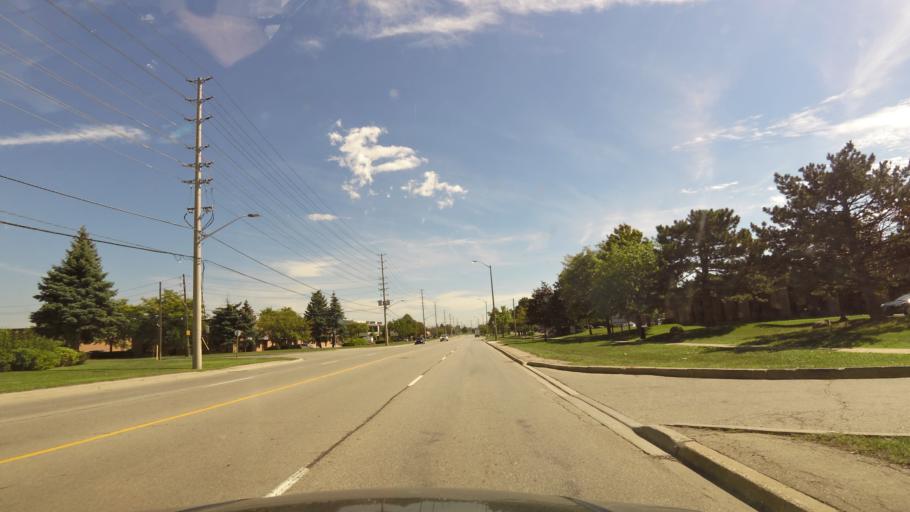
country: CA
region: Ontario
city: Mississauga
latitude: 43.6323
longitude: -79.6402
